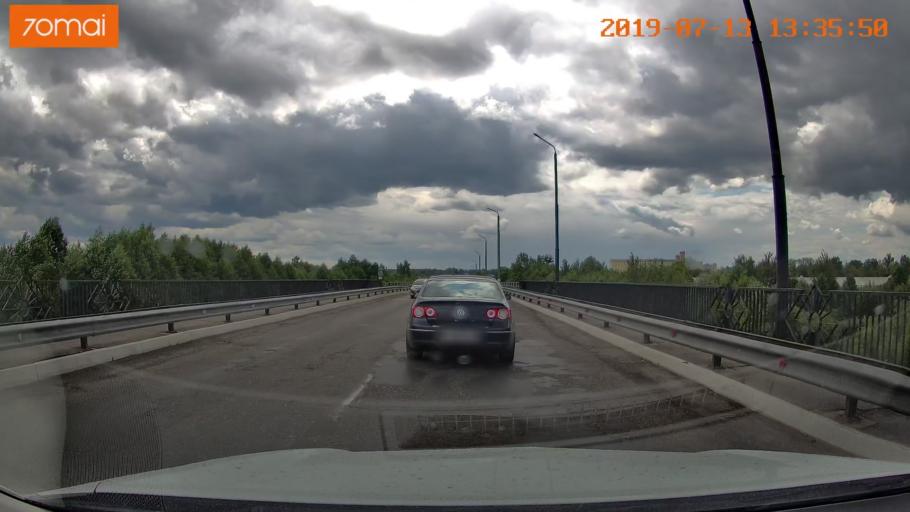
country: BY
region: Mogilev
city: Asipovichy
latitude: 53.3062
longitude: 28.6256
